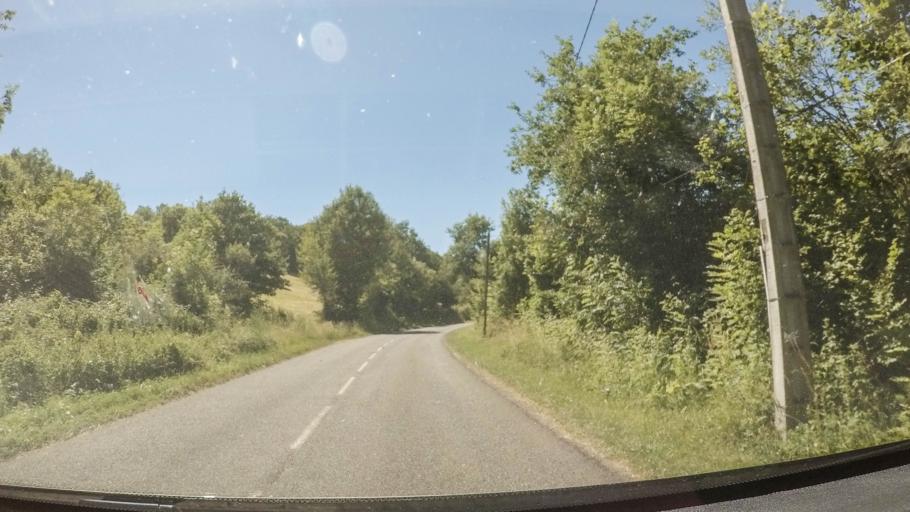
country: FR
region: Midi-Pyrenees
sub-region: Departement de l'Aveyron
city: Saint-Christophe-Vallon
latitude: 44.4646
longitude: 2.3814
